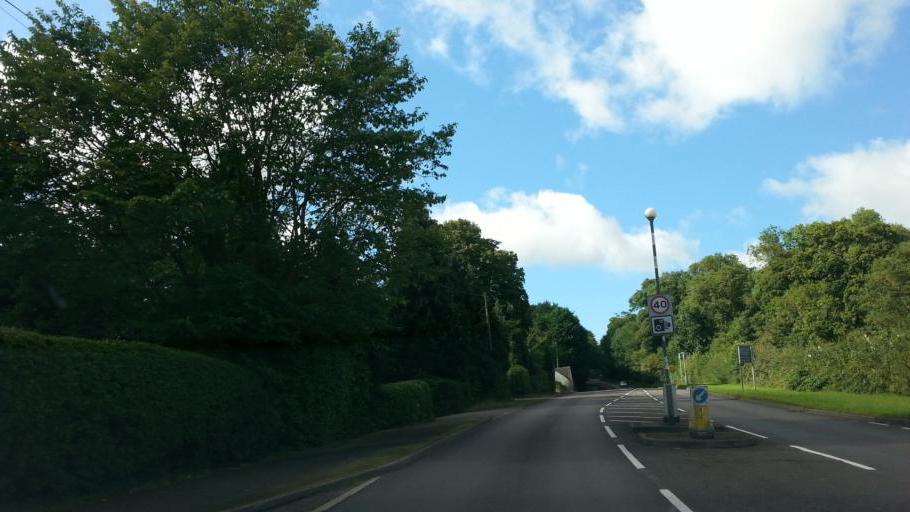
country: GB
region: England
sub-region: Staffordshire
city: Barton under Needwood
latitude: 52.8520
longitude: -1.7710
